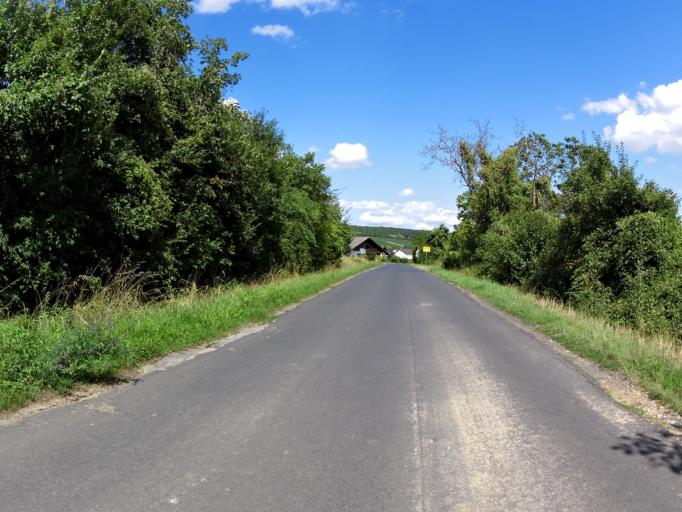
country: DE
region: Bavaria
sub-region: Regierungsbezirk Unterfranken
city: Prosselsheim
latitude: 49.8796
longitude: 10.1537
